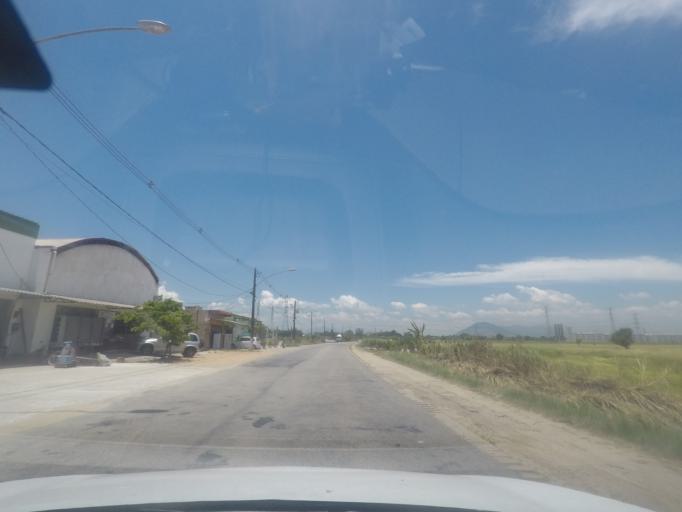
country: BR
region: Rio de Janeiro
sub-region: Itaguai
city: Itaguai
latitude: -22.9002
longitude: -43.6897
